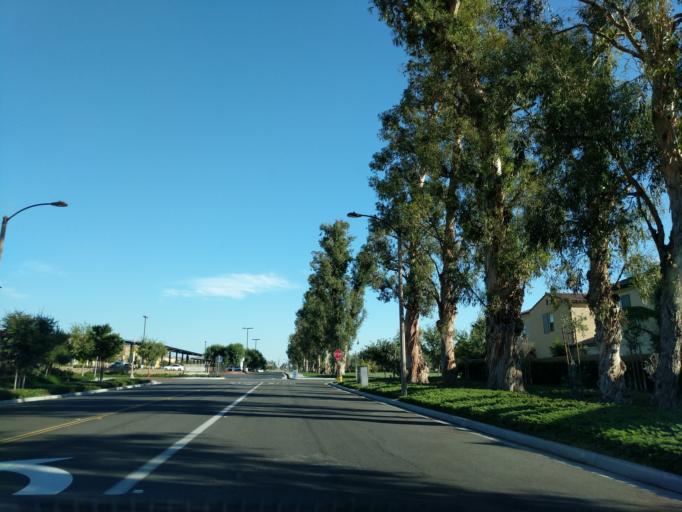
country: US
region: California
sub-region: Orange County
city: Irvine
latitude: 33.6861
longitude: -117.7607
